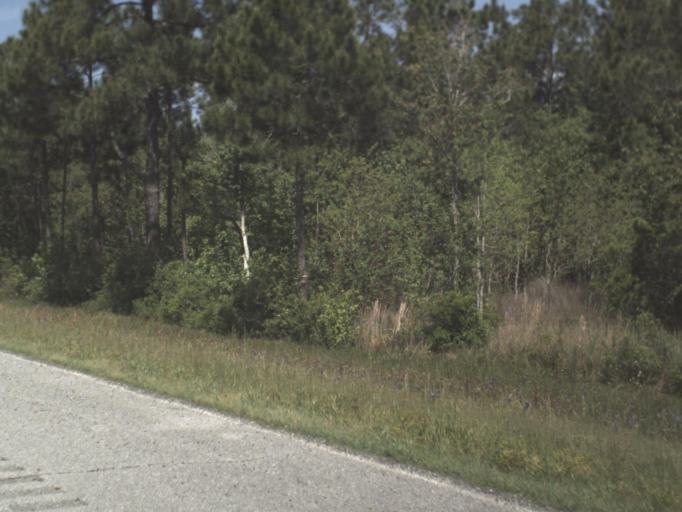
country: US
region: Florida
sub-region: Santa Rosa County
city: Pace
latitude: 30.5342
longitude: -87.1038
